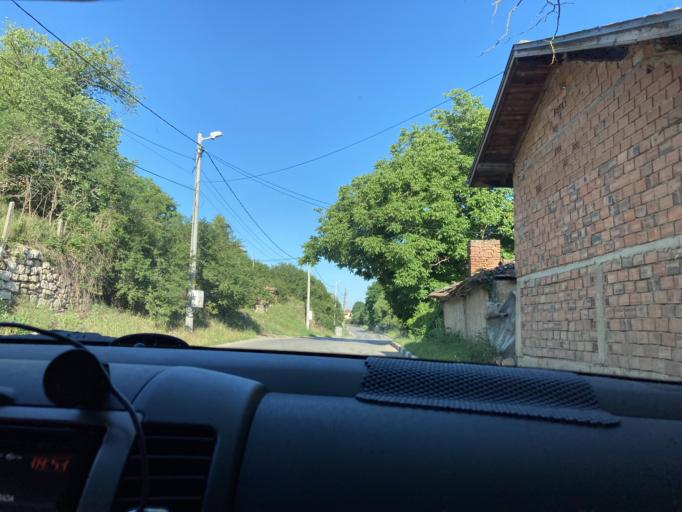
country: BG
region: Sofiya
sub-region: Obshtina Slivnitsa
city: Slivnitsa
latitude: 42.8465
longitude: 22.9932
